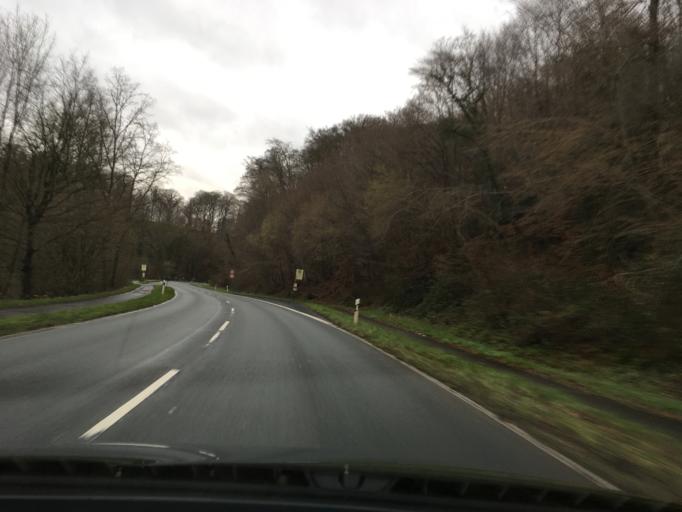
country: DE
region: North Rhine-Westphalia
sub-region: Regierungsbezirk Dusseldorf
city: Mettmann
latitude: 51.2286
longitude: 6.9615
